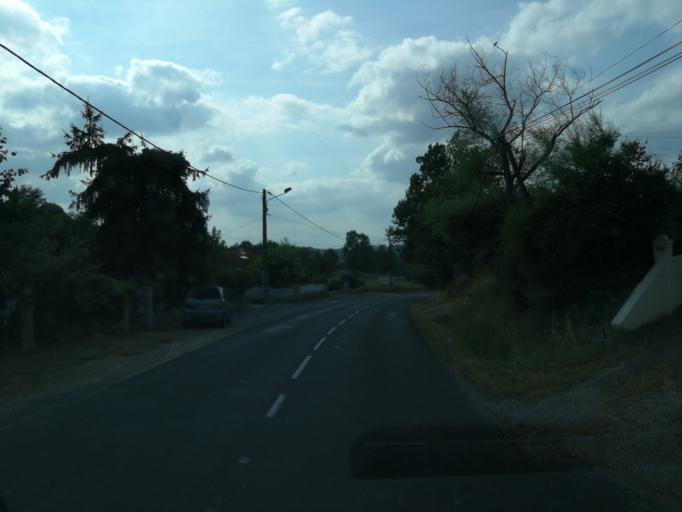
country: FR
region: Aquitaine
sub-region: Departement du Lot-et-Garonne
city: Fumel
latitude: 44.5037
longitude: 0.9527
